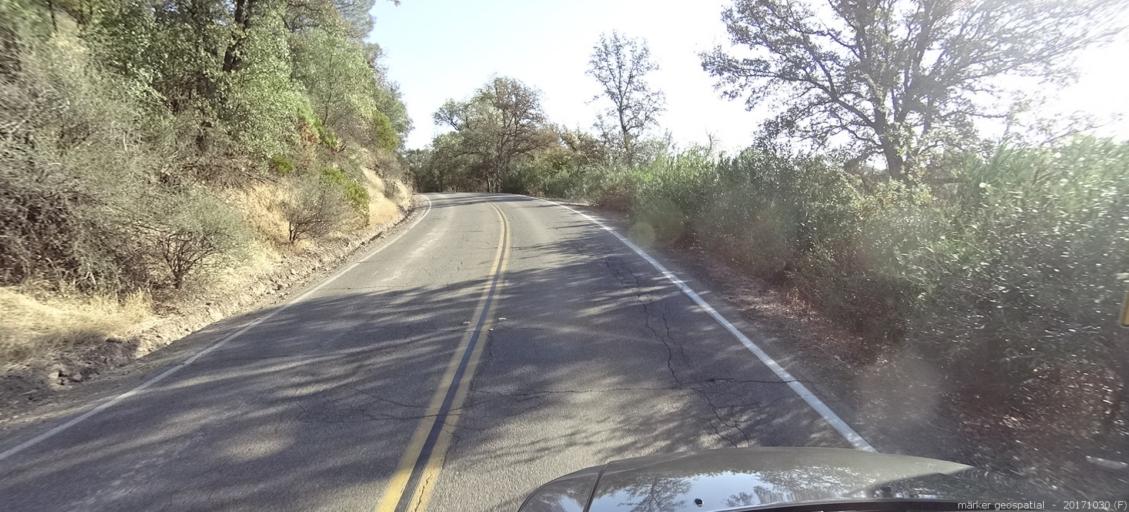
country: US
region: California
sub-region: Shasta County
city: Palo Cedro
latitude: 40.5650
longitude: -122.2154
